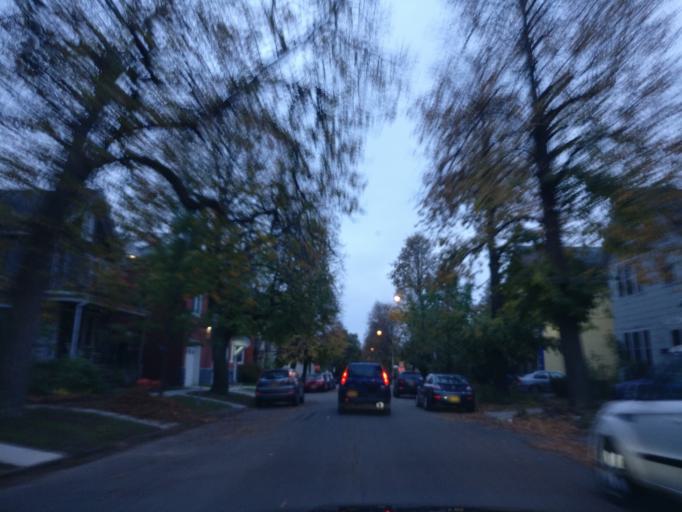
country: US
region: New York
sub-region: Erie County
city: Buffalo
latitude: 42.9021
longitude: -78.8877
